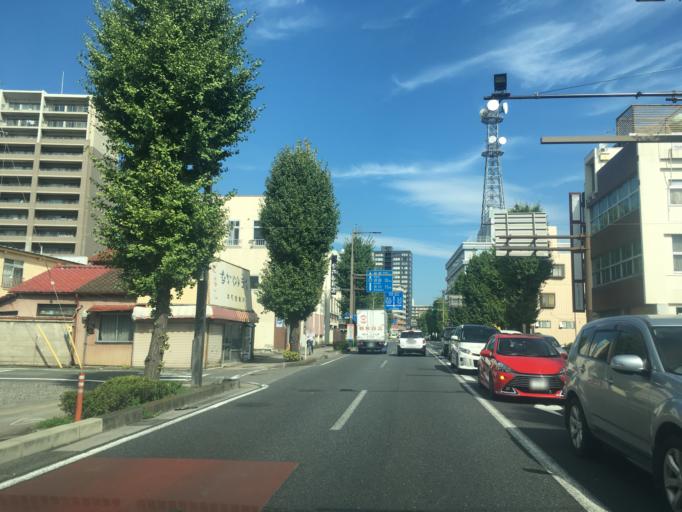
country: JP
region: Gunma
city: Maebashi-shi
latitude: 36.3883
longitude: 139.0676
